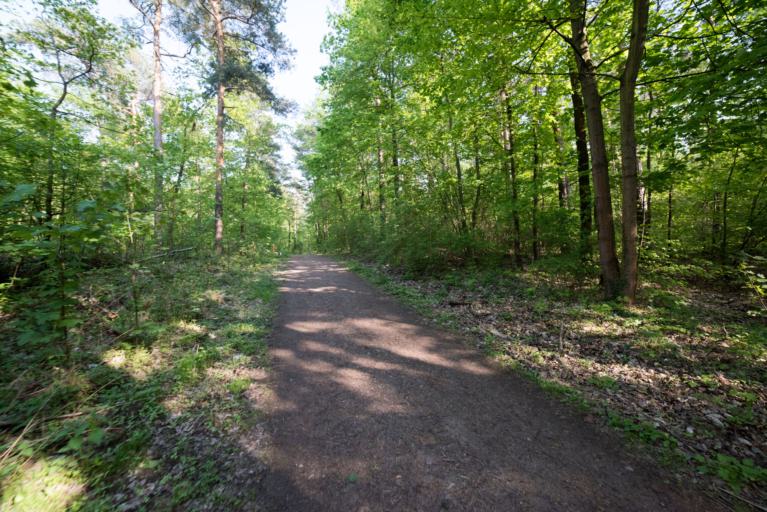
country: DE
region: Saxony
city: Albertstadt
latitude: 51.0806
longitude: 13.7789
